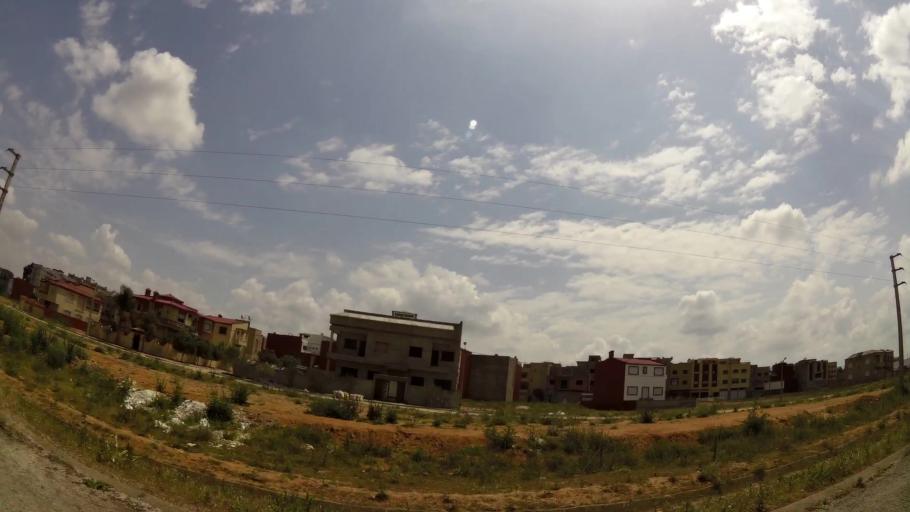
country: MA
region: Gharb-Chrarda-Beni Hssen
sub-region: Kenitra Province
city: Kenitra
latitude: 34.0102
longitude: -6.5403
